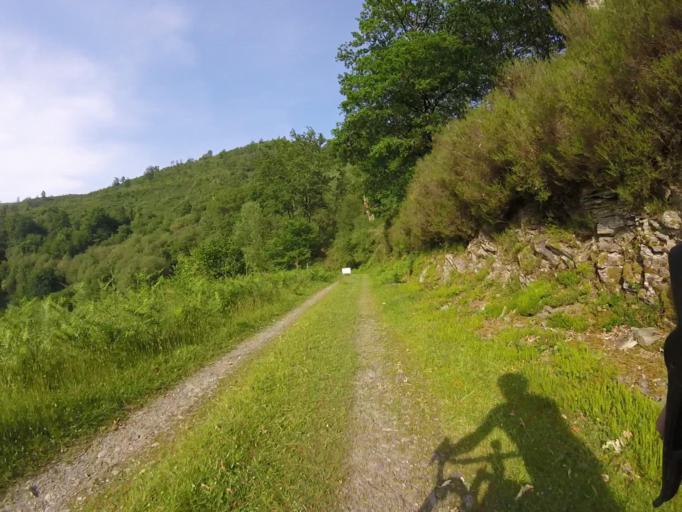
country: ES
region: Navarre
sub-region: Provincia de Navarra
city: Arano
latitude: 43.2235
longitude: -1.8646
